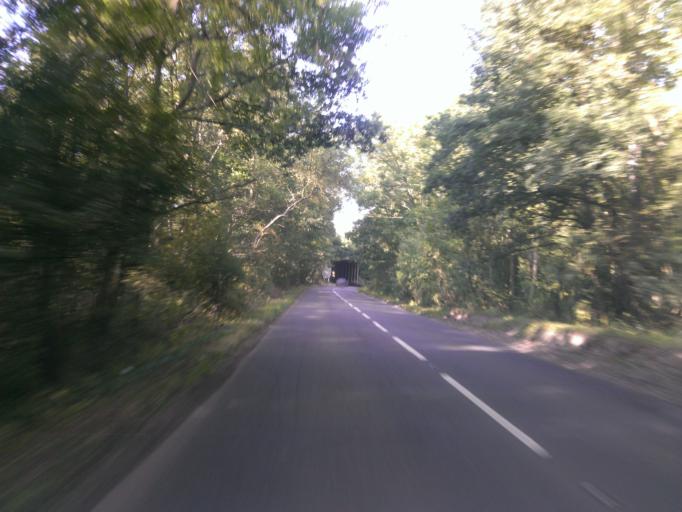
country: GB
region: England
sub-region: Kent
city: Tonbridge
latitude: 51.2079
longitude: 0.2246
